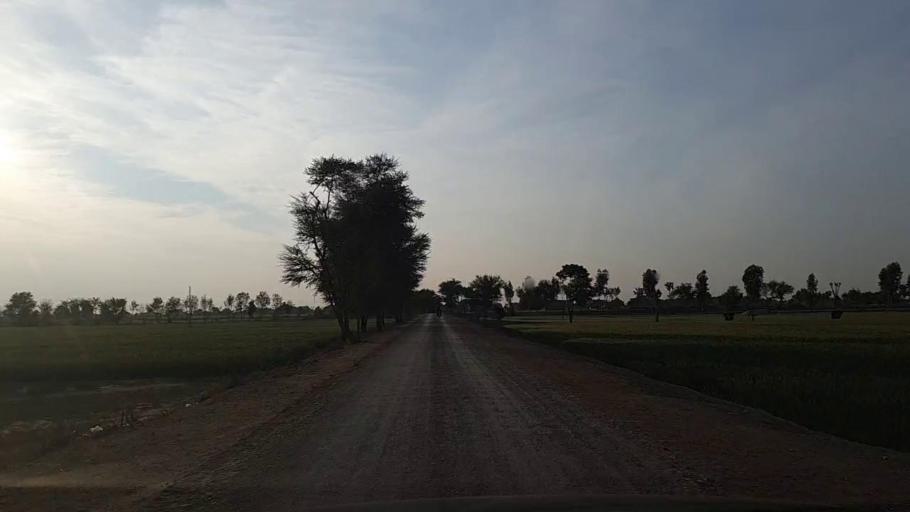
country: PK
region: Sindh
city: Jam Sahib
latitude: 26.4320
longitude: 68.5675
